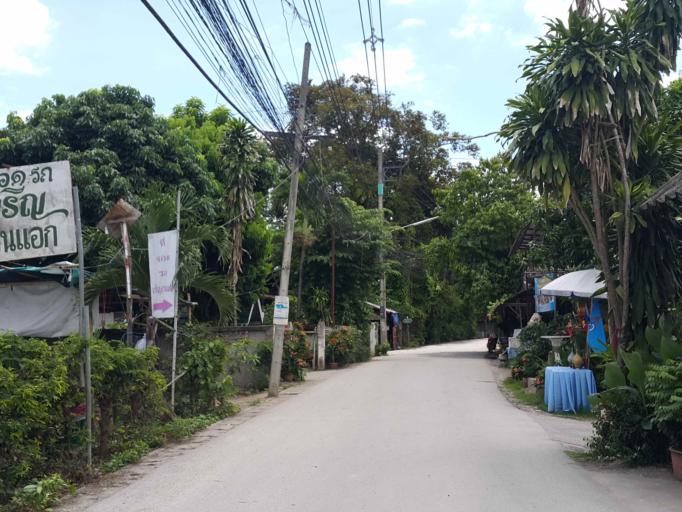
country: TH
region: Chiang Mai
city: Chiang Mai
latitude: 18.8258
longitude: 99.0037
